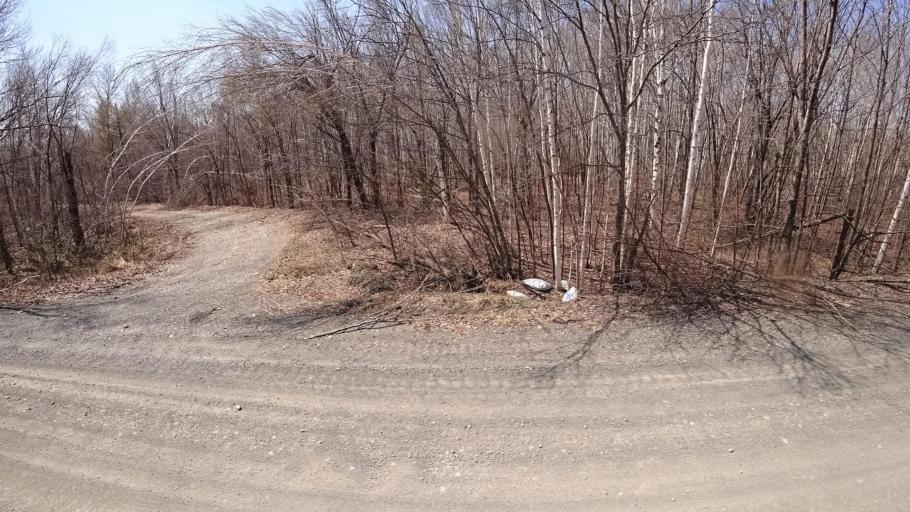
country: RU
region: Khabarovsk Krai
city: Khurba
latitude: 50.4107
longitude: 136.8438
